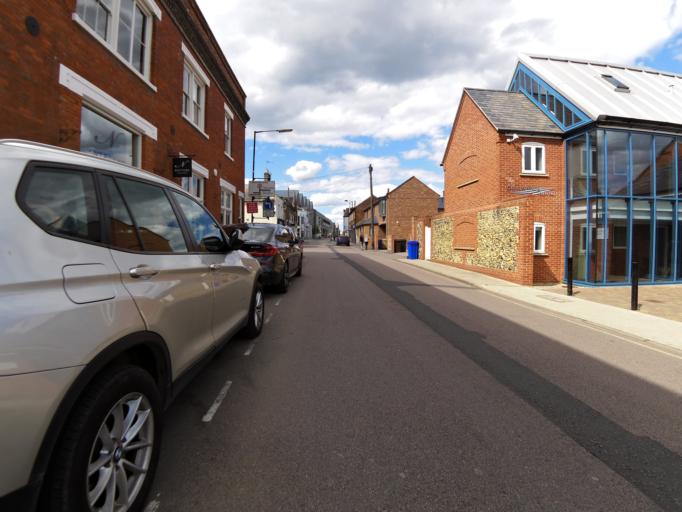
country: GB
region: England
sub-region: Suffolk
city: Bury St Edmunds
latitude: 52.2441
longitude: 0.7111
